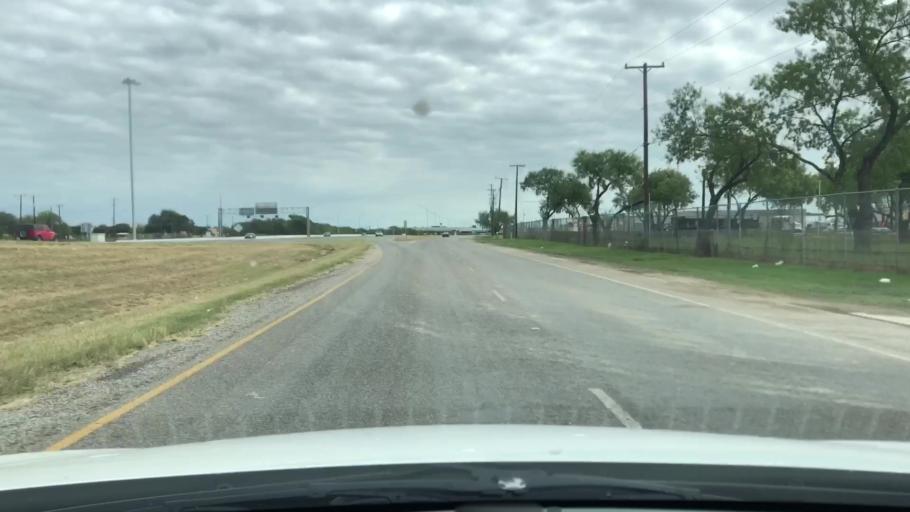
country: US
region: Texas
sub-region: Bexar County
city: Lackland Air Force Base
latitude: 29.4071
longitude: -98.5980
